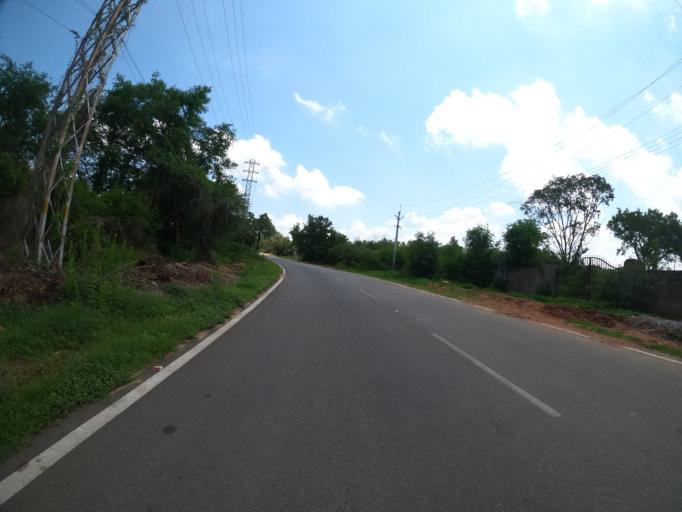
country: IN
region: Telangana
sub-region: Rangareddi
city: Sriramnagar
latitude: 17.3672
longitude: 78.3253
